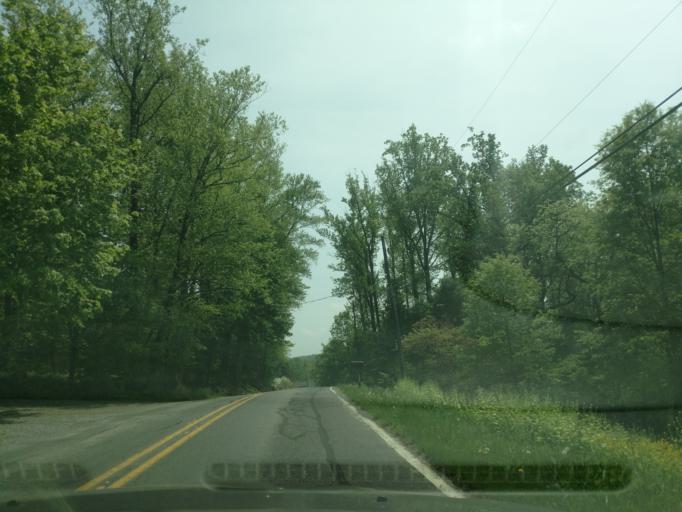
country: US
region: Pennsylvania
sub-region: Chester County
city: Elverson
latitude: 40.1667
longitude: -75.8326
